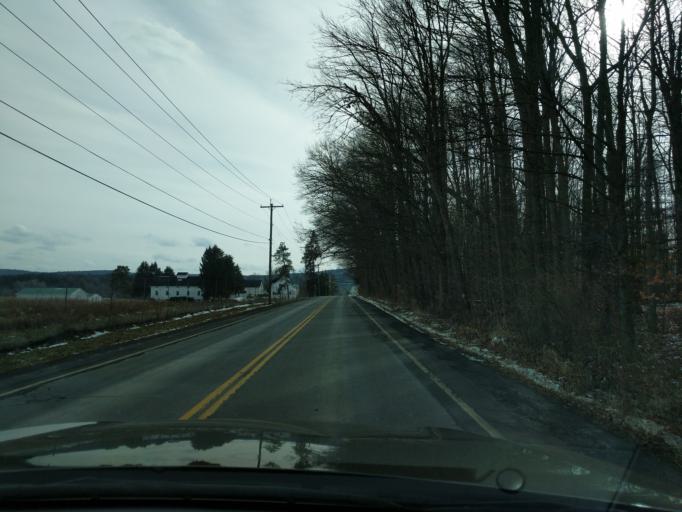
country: US
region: New York
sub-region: Tompkins County
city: Northeast Ithaca
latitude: 42.4476
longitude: -76.4492
